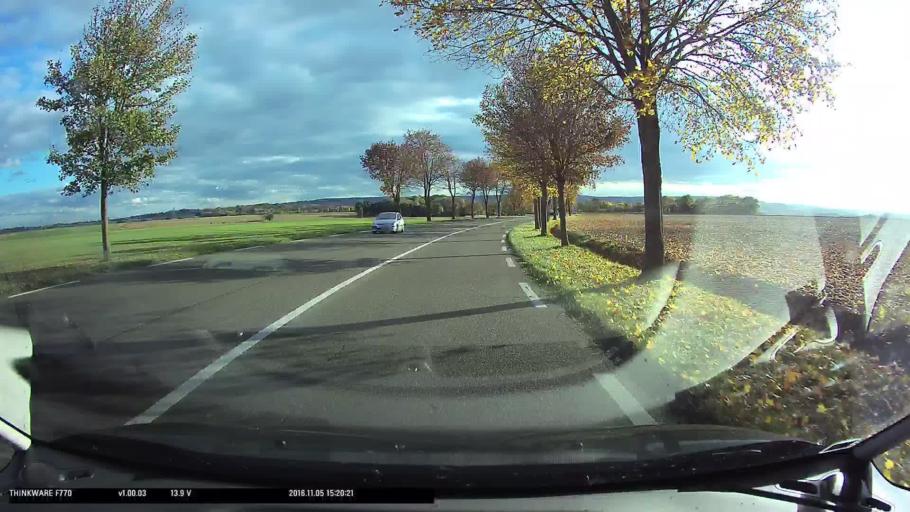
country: FR
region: Ile-de-France
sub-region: Departement du Val-d'Oise
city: Sagy
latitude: 49.0645
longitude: 1.9617
